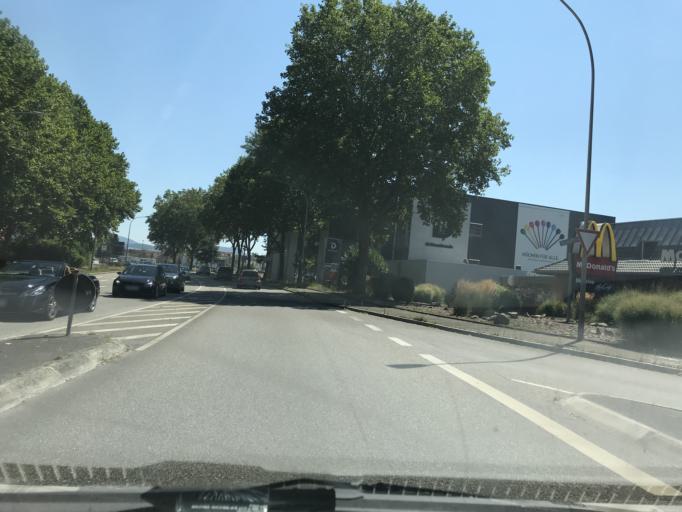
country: CH
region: Aargau
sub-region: Bezirk Rheinfelden
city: Mumpf
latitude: 47.5546
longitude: 7.9305
